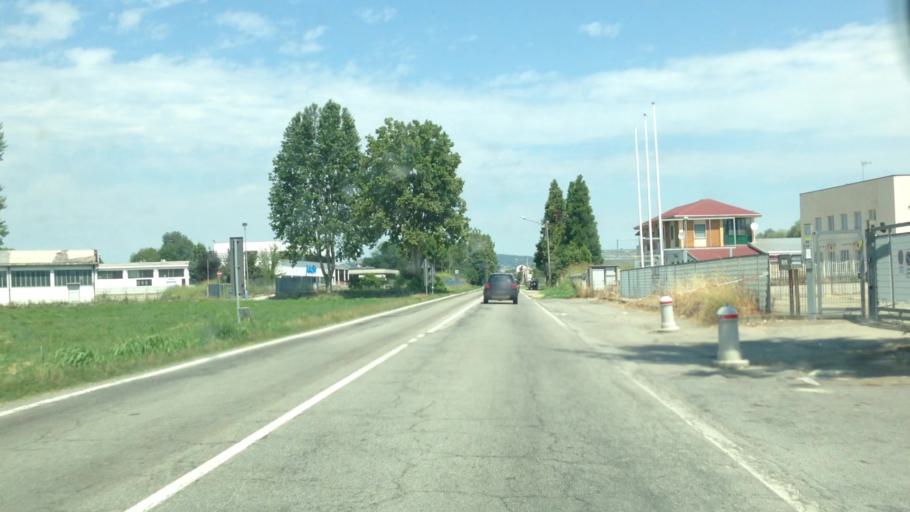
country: IT
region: Piedmont
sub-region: Provincia di Asti
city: Castell'Alfero
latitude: 44.9804
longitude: 8.2264
